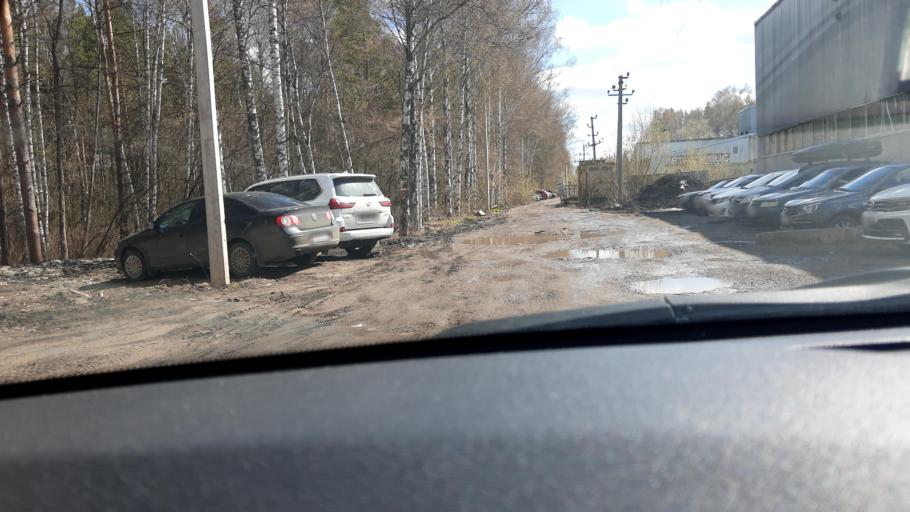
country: RU
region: Bashkortostan
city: Ufa
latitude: 54.6965
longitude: 55.9339
